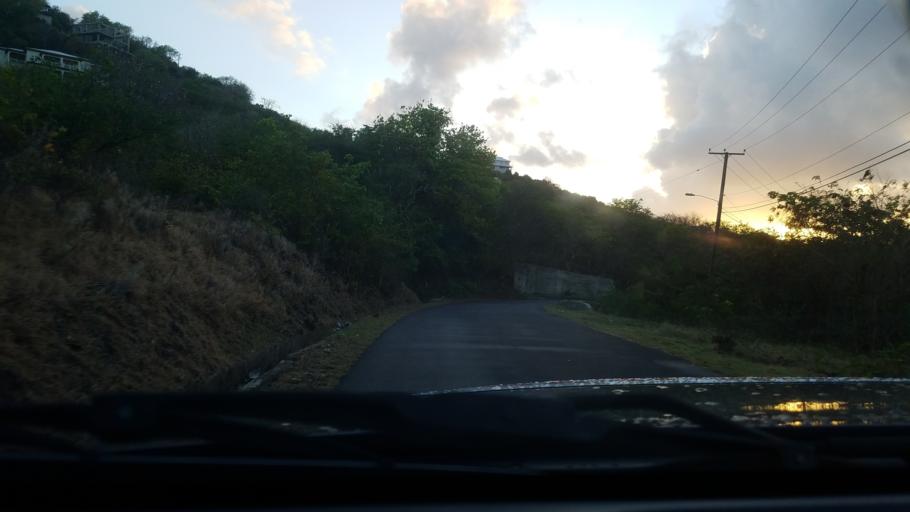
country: LC
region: Gros-Islet
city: Gros Islet
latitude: 14.0899
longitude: -60.9356
